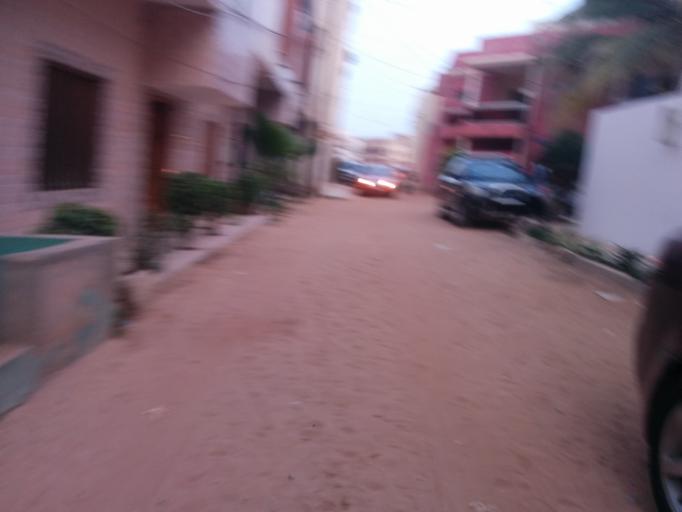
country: SN
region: Dakar
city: Grand Dakar
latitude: 14.7627
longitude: -17.4513
